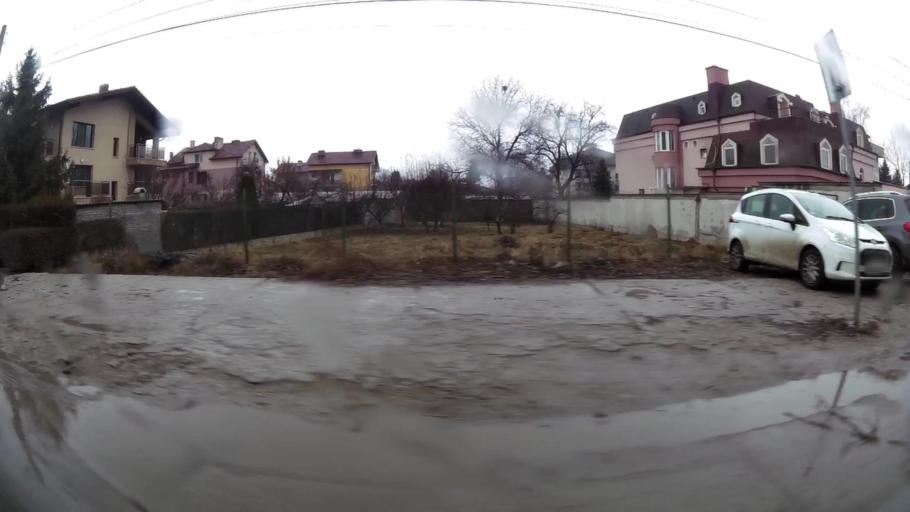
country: BG
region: Sofia-Capital
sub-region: Stolichna Obshtina
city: Sofia
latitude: 42.6340
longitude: 23.4096
